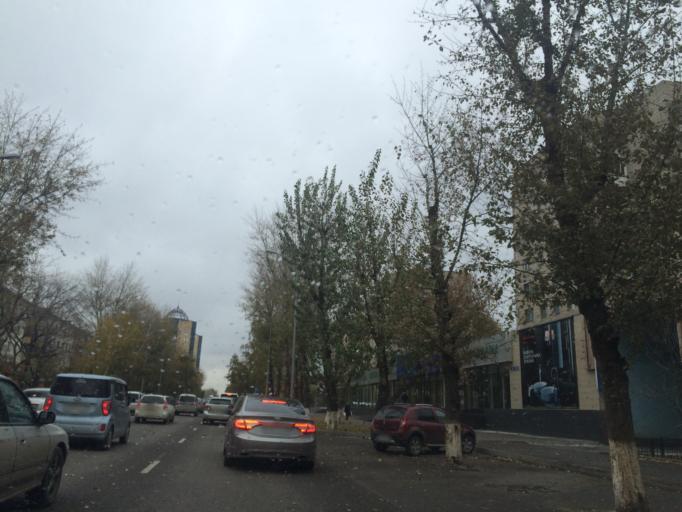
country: KZ
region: Astana Qalasy
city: Astana
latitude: 51.1693
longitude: 71.4348
